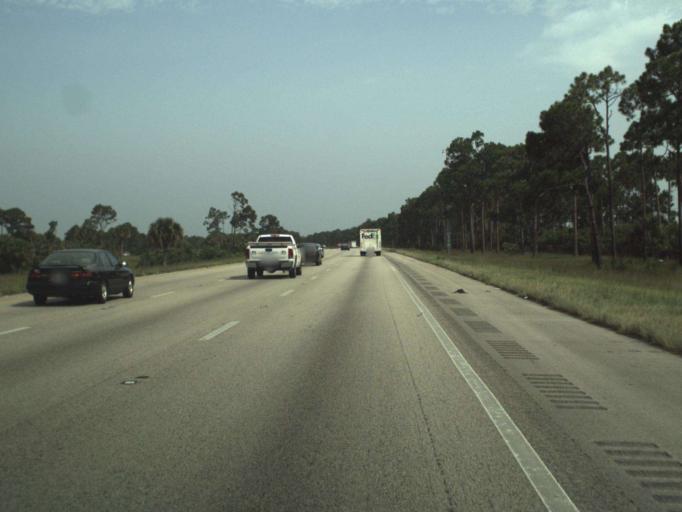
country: US
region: Florida
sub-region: Saint Lucie County
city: Port Saint Lucie
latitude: 27.2425
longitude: -80.4136
